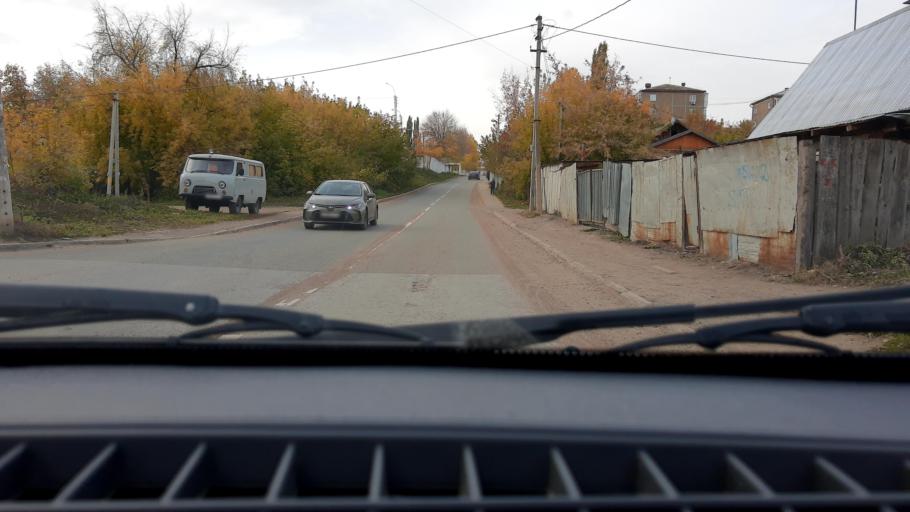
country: RU
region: Bashkortostan
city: Ufa
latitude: 54.8175
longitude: 56.1300
